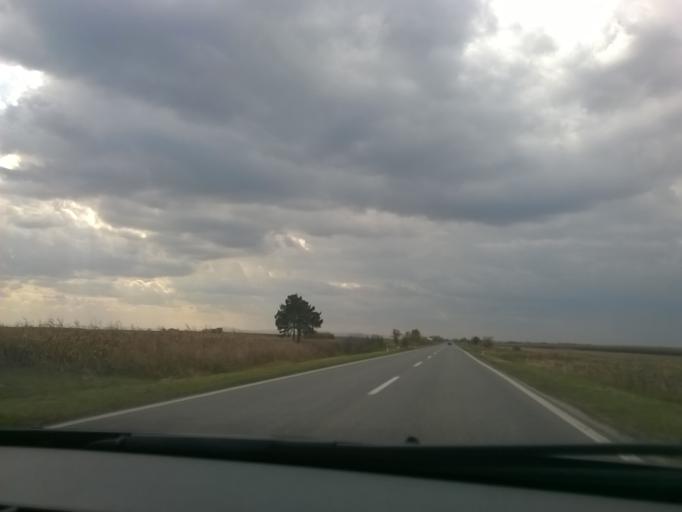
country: RS
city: Vladimirovac
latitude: 45.0070
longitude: 20.8135
